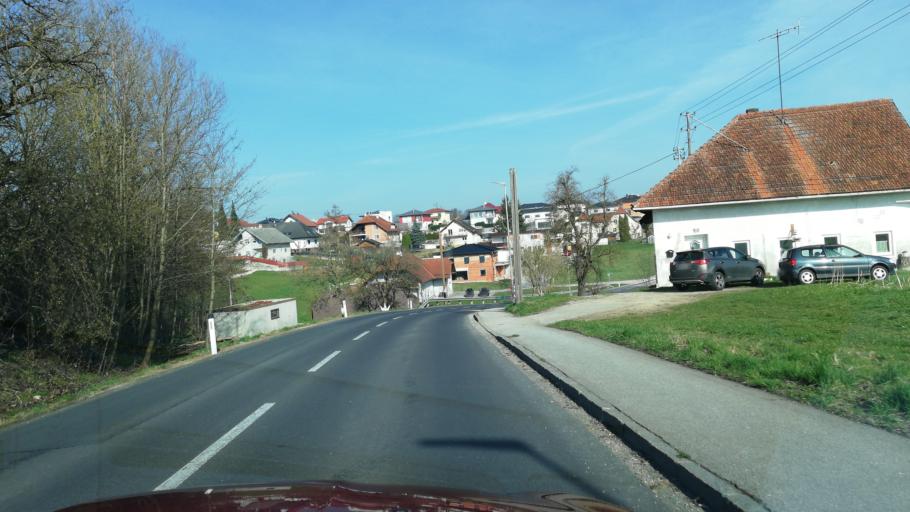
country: AT
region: Upper Austria
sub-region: Politischer Bezirk Kirchdorf an der Krems
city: Kremsmunster
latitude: 48.0602
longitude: 14.1243
